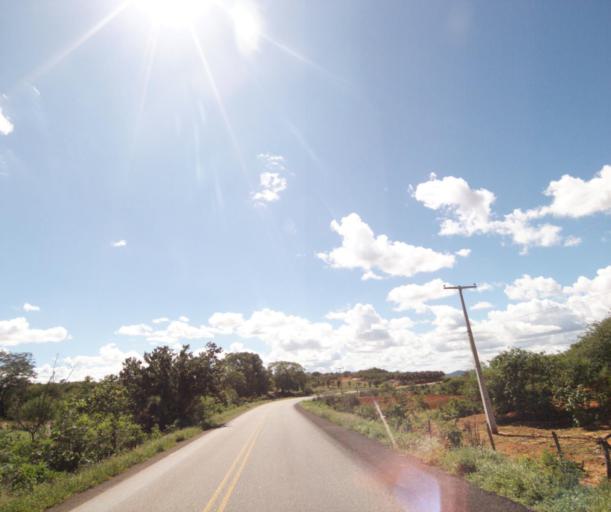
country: BR
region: Bahia
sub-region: Cacule
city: Cacule
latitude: -14.1911
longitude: -42.1563
